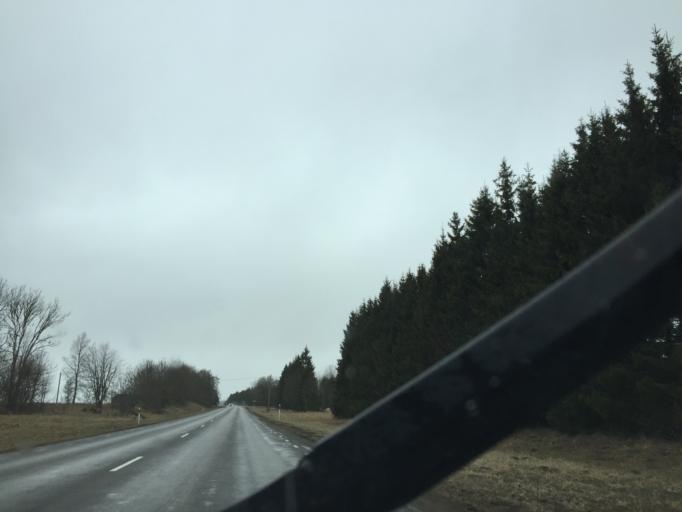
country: EE
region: Laeaene
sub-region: Ridala Parish
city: Uuemoisa
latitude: 58.8761
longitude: 23.6109
